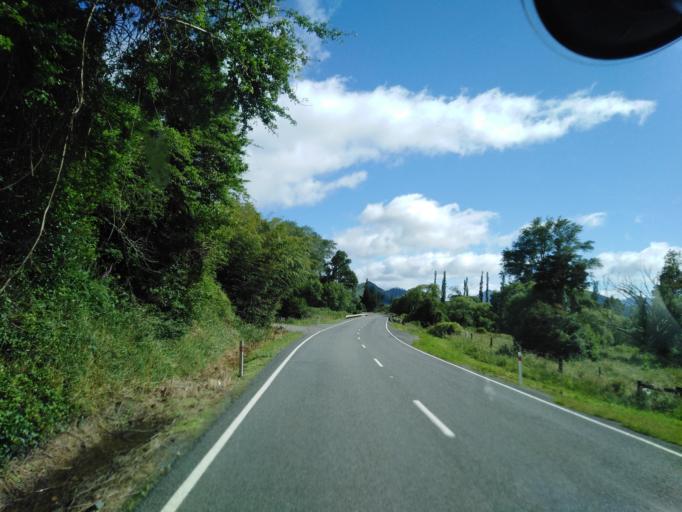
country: NZ
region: Nelson
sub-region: Nelson City
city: Nelson
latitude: -41.2508
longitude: 173.5775
